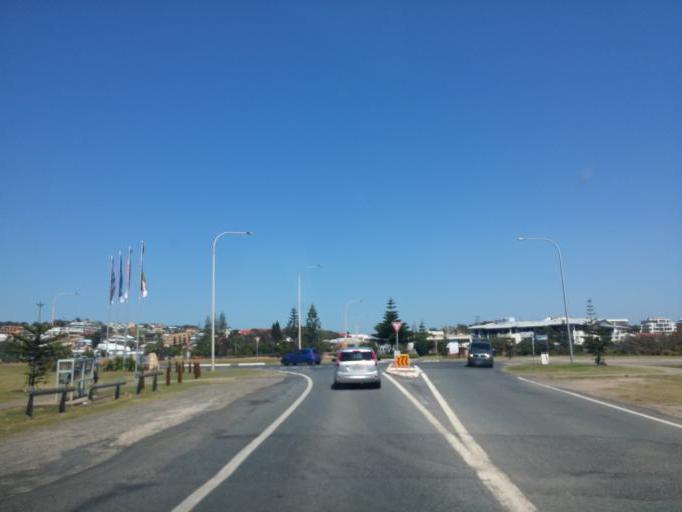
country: AU
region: New South Wales
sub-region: Coffs Harbour
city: Coffs Harbour
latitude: -30.3024
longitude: 153.1404
